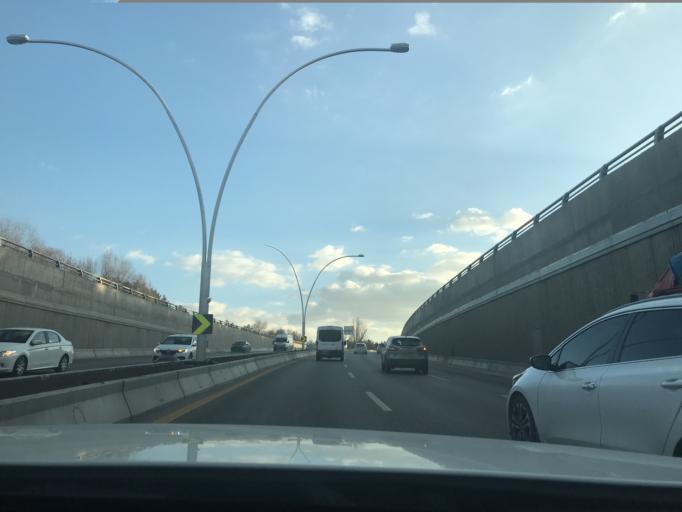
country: TR
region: Ankara
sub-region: Goelbasi
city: Golbasi
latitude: 39.8487
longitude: 32.8108
